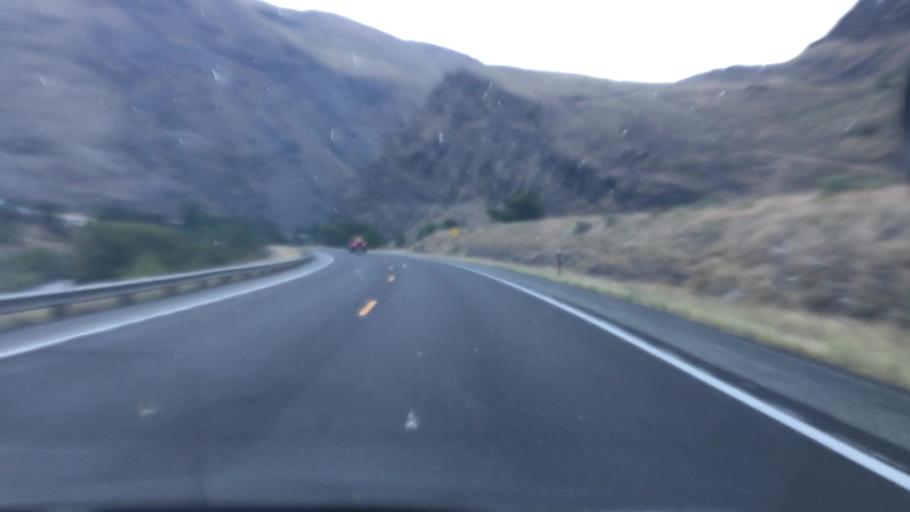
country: US
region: Idaho
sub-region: Valley County
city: McCall
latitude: 45.3527
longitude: -116.3569
